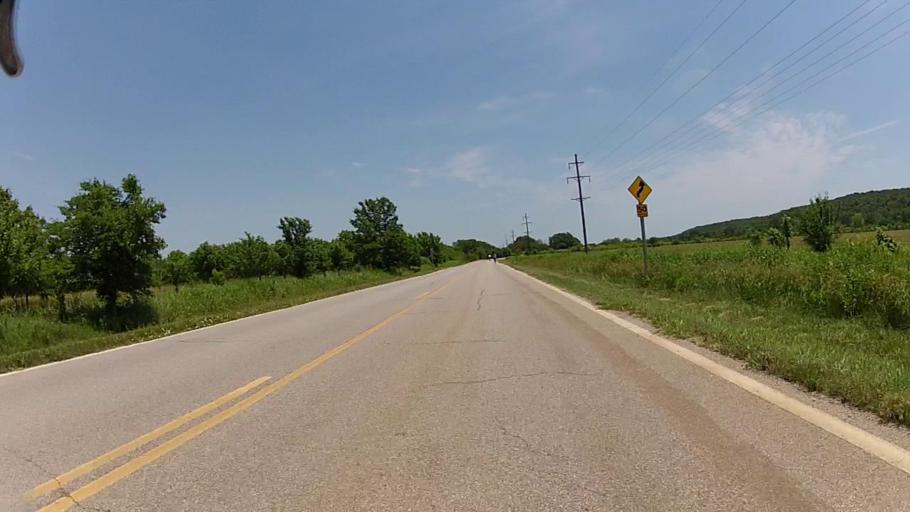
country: US
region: Kansas
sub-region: Chautauqua County
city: Sedan
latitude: 37.1201
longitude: -96.2266
